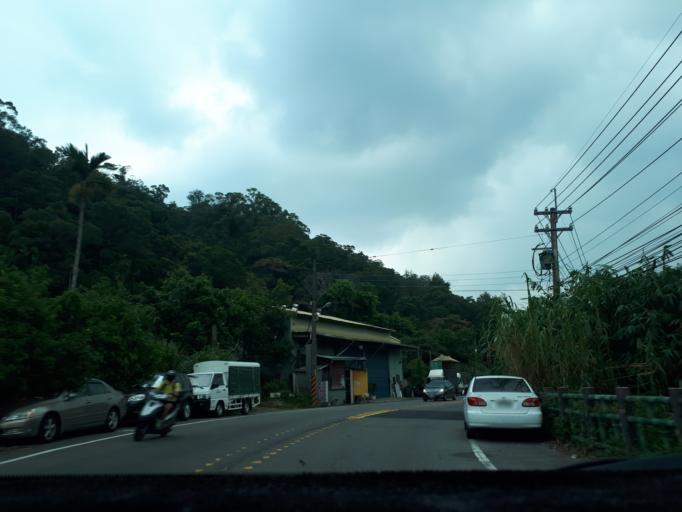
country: TW
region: Taipei
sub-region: Taipei
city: Banqiao
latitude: 24.9481
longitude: 121.4803
